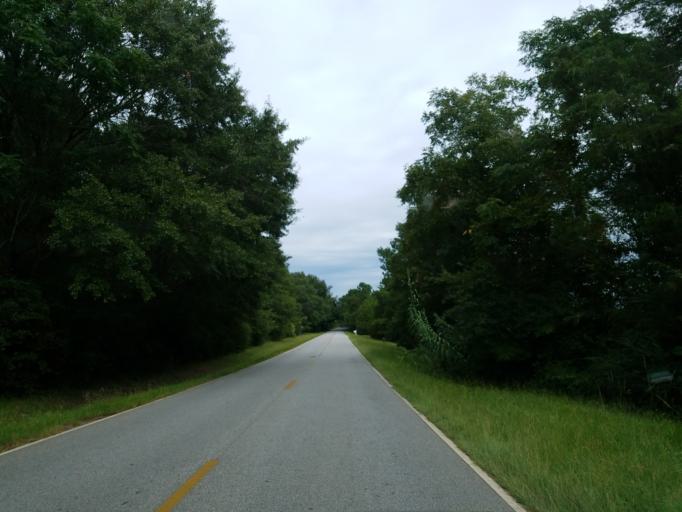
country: US
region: Georgia
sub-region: Lamar County
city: Barnesville
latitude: 33.0113
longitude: -84.1158
